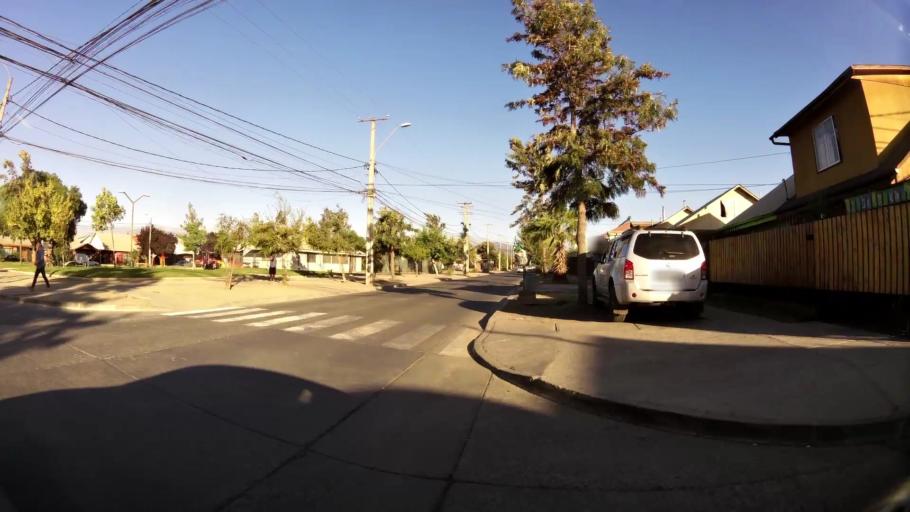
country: CL
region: O'Higgins
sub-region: Provincia de Cachapoal
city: Rancagua
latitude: -34.1730
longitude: -70.7653
